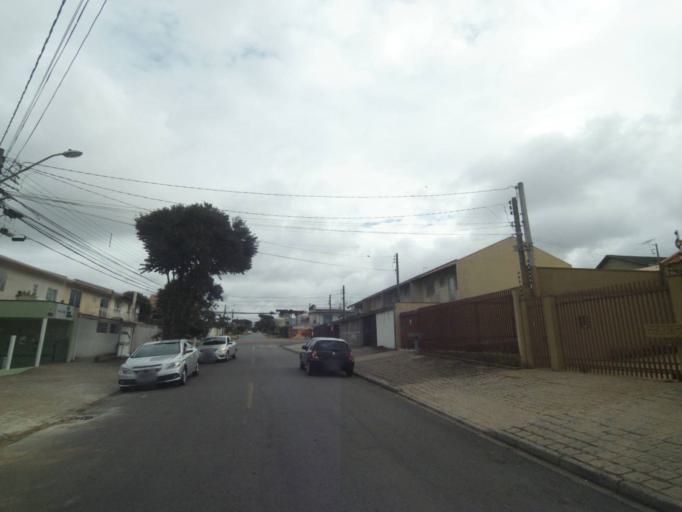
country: BR
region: Parana
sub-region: Curitiba
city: Curitiba
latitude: -25.4920
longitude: -49.3075
